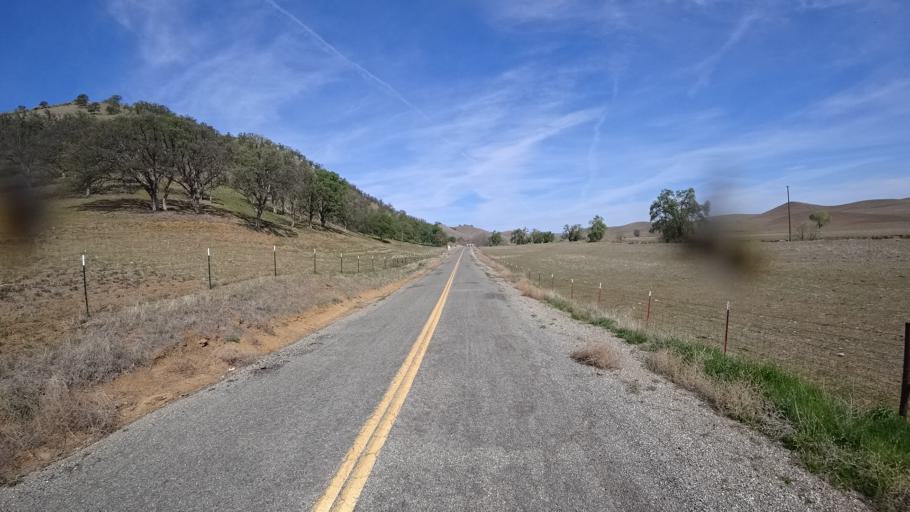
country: US
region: California
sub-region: Glenn County
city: Willows
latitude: 39.5424
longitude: -122.3969
